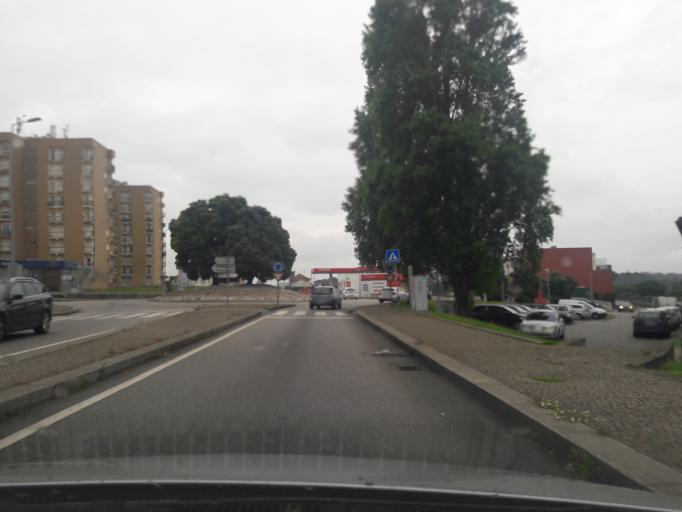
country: PT
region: Porto
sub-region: Vila do Conde
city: Vila do Conde
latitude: 41.3422
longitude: -8.7348
